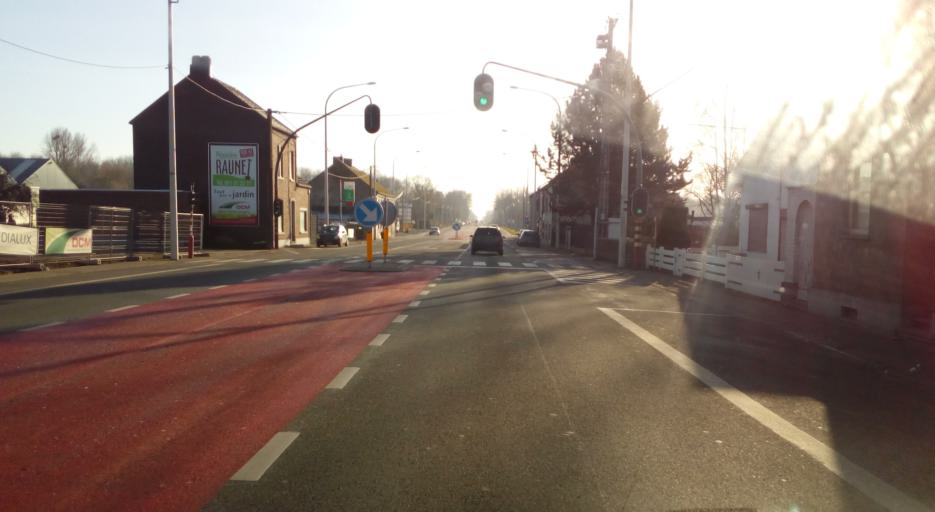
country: BE
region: Wallonia
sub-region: Province du Hainaut
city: Gerpinnes
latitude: 50.3382
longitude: 4.4742
